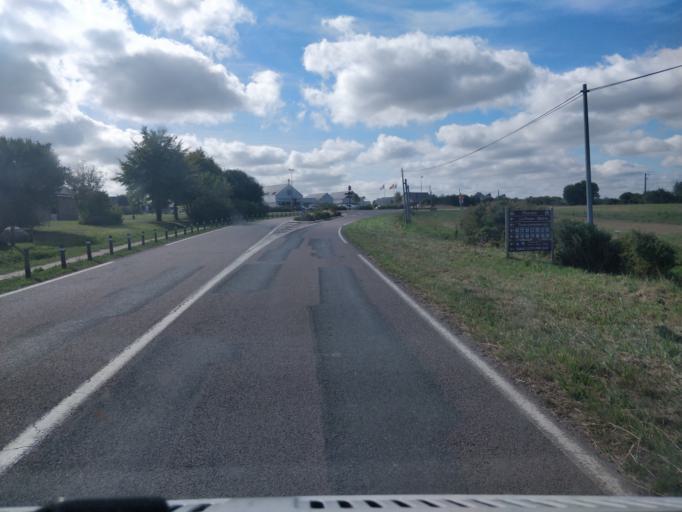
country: FR
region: Brittany
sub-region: Departement des Cotes-d'Armor
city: Plurien
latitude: 48.6254
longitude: -2.4098
